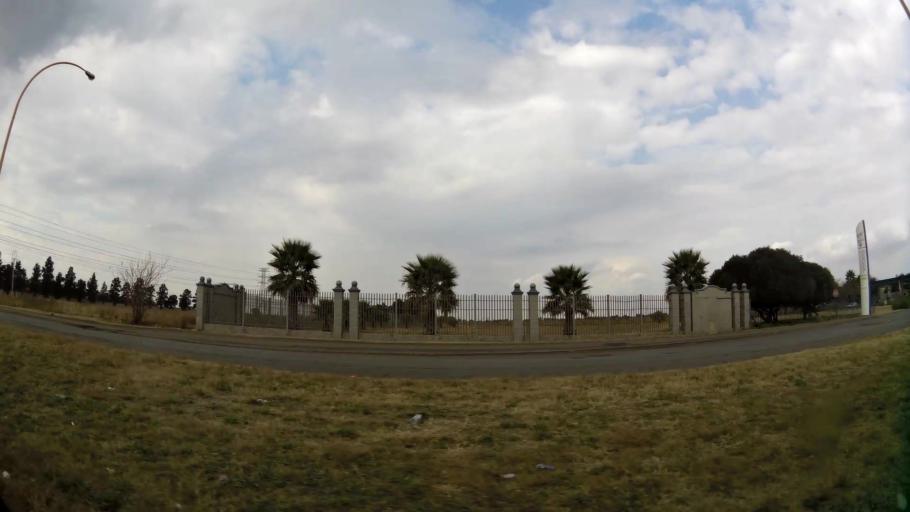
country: ZA
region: Gauteng
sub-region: Sedibeng District Municipality
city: Vanderbijlpark
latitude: -26.6742
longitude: 27.8182
